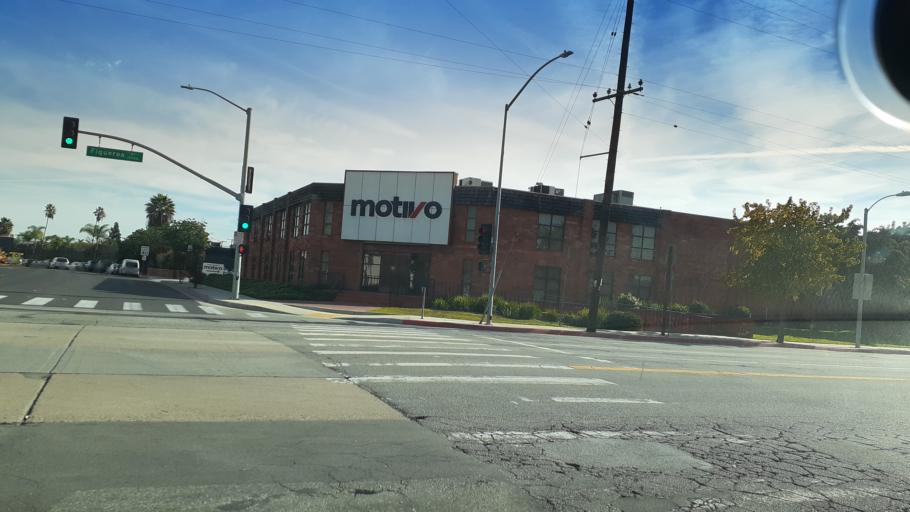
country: US
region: California
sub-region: Los Angeles County
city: West Rancho Dominguez
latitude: 33.8703
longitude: -118.2818
